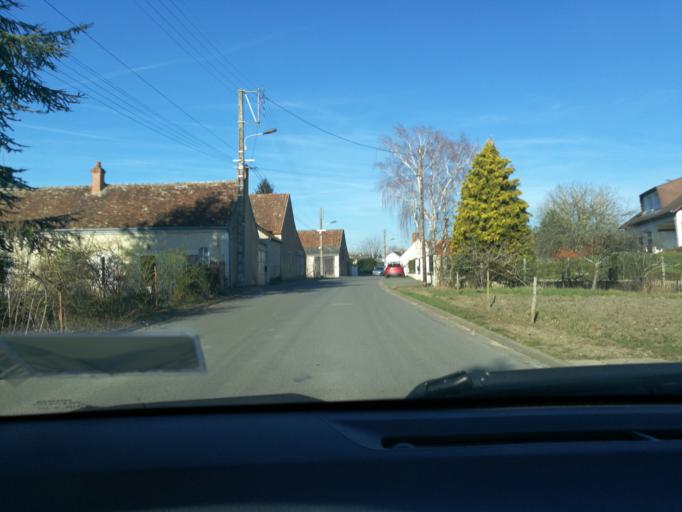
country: FR
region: Centre
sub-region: Departement du Loiret
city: Chaingy
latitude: 47.8807
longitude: 1.7708
